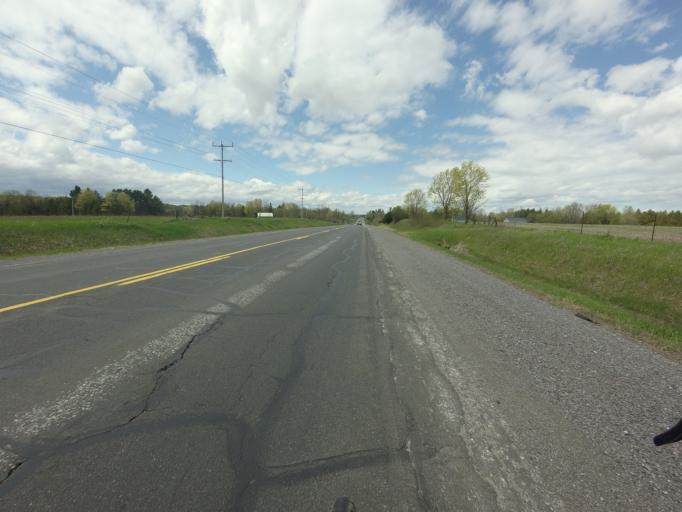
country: CA
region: Ontario
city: Carleton Place
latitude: 45.2517
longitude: -76.2447
